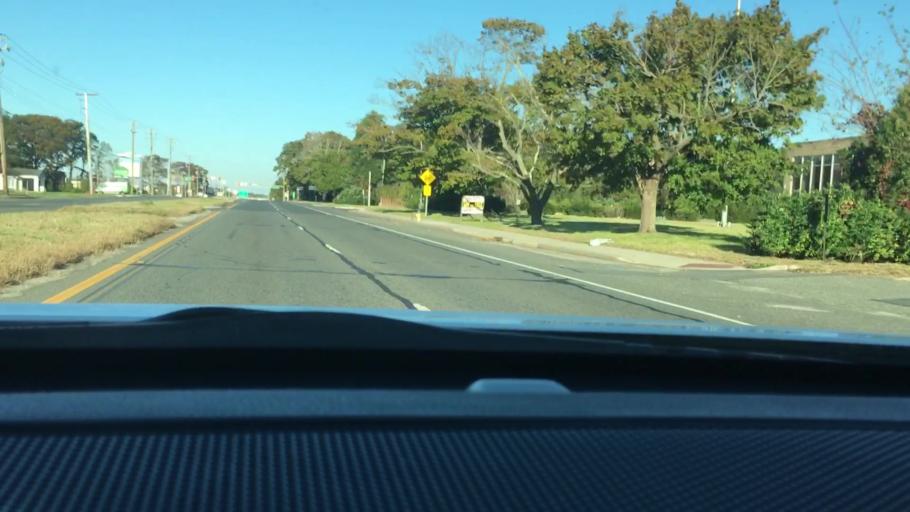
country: US
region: New Jersey
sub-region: Atlantic County
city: Pleasantville
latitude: 39.3964
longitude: -74.5471
